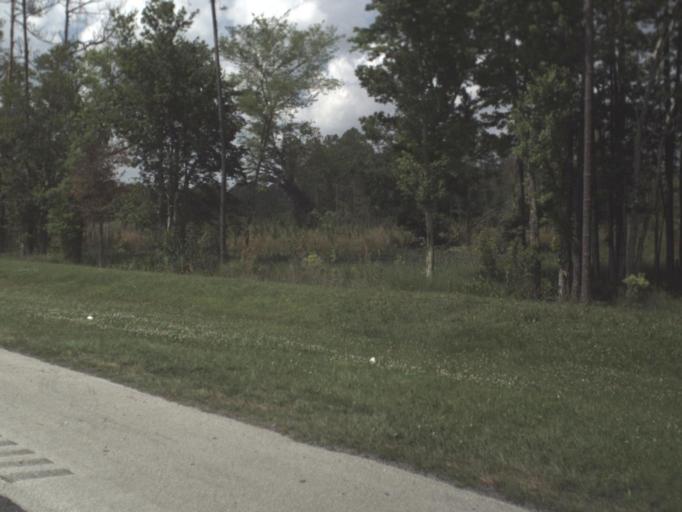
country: US
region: Florida
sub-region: Saint Johns County
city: Saint Augustine
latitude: 29.9548
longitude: -81.4426
